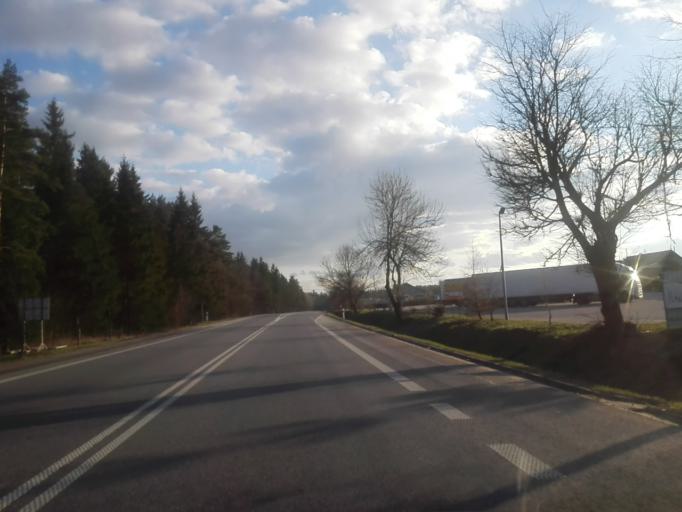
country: PL
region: Podlasie
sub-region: Suwalki
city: Suwalki
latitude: 54.1592
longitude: 22.9783
